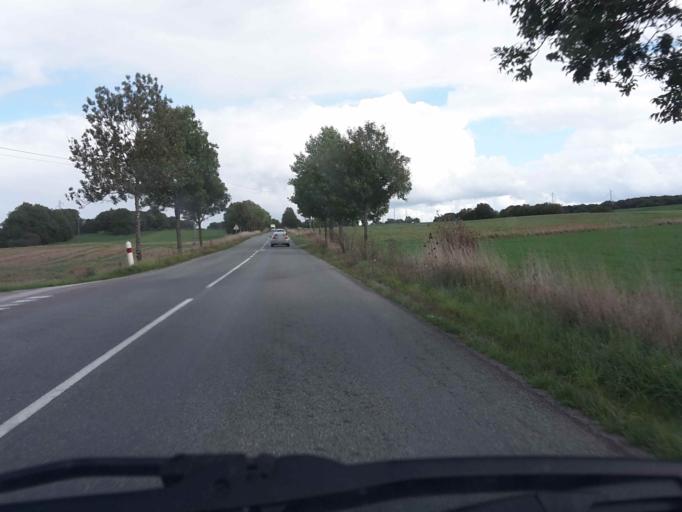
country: FR
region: Franche-Comte
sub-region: Departement du Doubs
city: Saone
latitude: 47.2412
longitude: 6.1280
